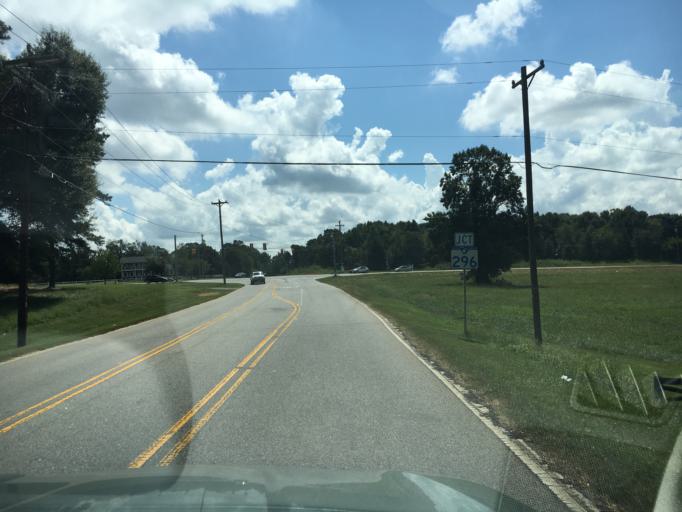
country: US
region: South Carolina
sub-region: Spartanburg County
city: Fairforest
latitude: 34.9012
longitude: -82.0373
